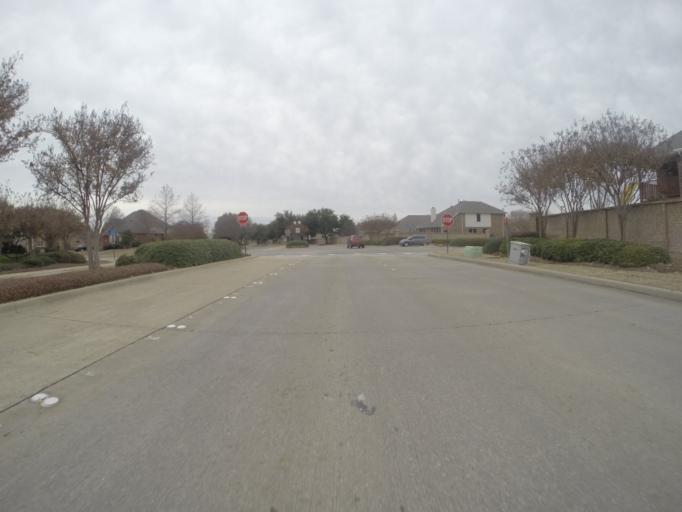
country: US
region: Texas
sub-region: Collin County
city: Saint Paul
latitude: 33.0346
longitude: -96.5686
